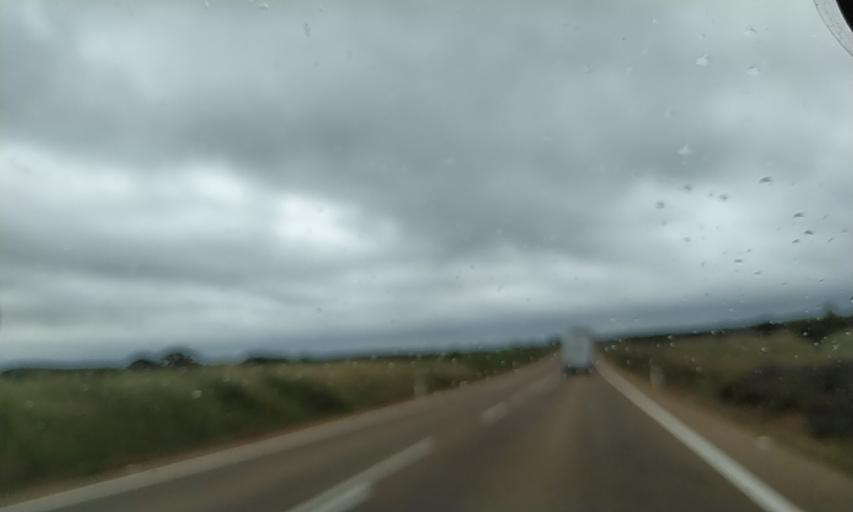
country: ES
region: Extremadura
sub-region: Provincia de Badajoz
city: Villar del Rey
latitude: 39.0152
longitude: -6.8520
